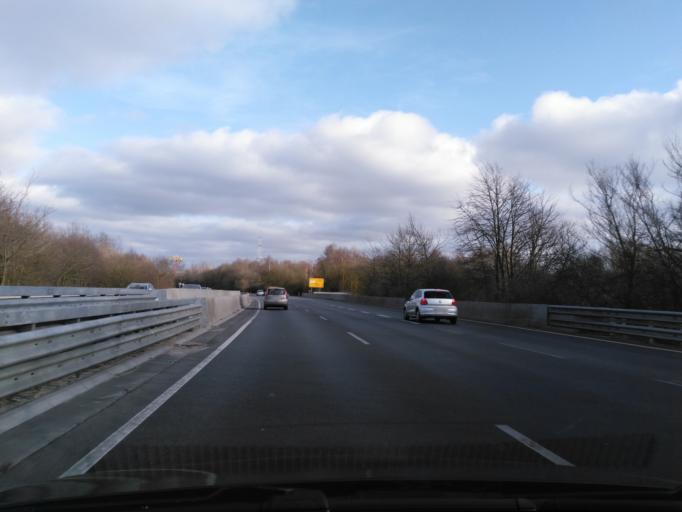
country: DE
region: Schleswig-Holstein
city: Klausdorf
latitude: 54.2920
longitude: 10.2068
